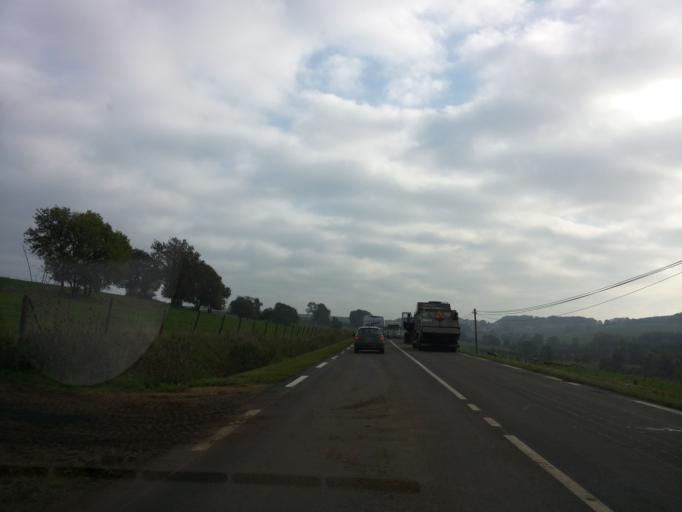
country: FR
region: Lorraine
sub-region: Departement de la Meuse
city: Montmedy
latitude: 49.5832
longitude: 5.2916
